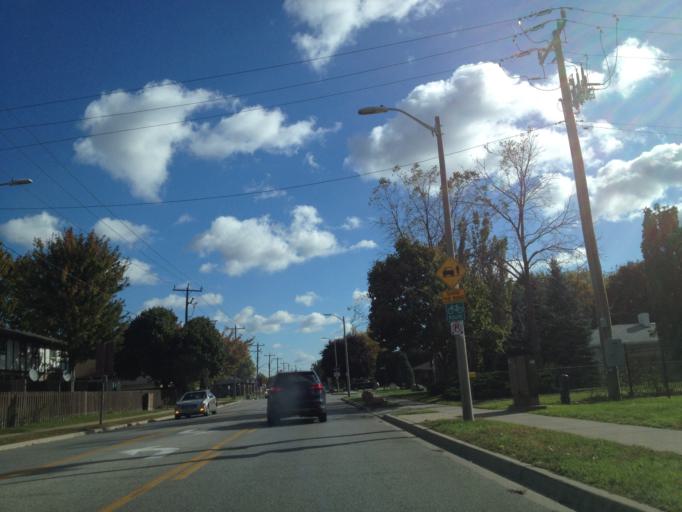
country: CA
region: Ontario
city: Amherstburg
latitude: 42.0460
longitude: -82.5859
